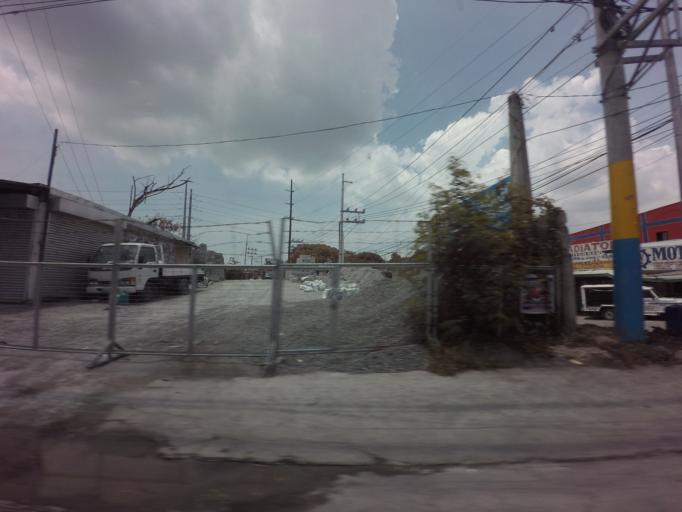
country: PH
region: Calabarzon
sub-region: Province of Laguna
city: San Pedro
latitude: 14.3992
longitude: 121.0464
